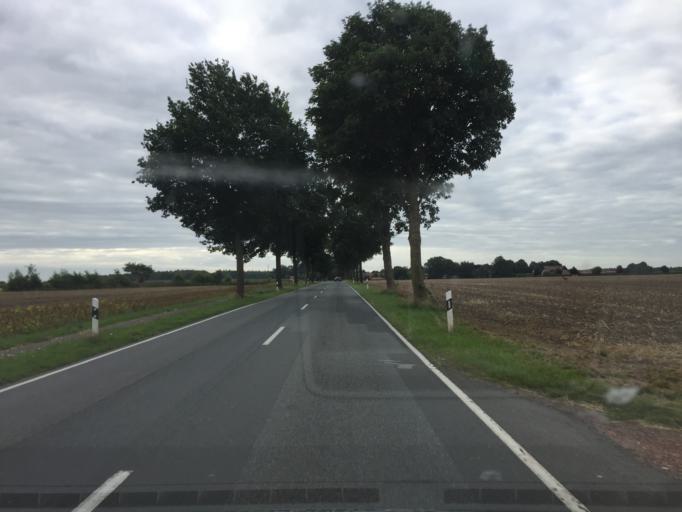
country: DE
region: Lower Saxony
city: Ehrenburg
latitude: 52.7430
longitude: 8.7125
